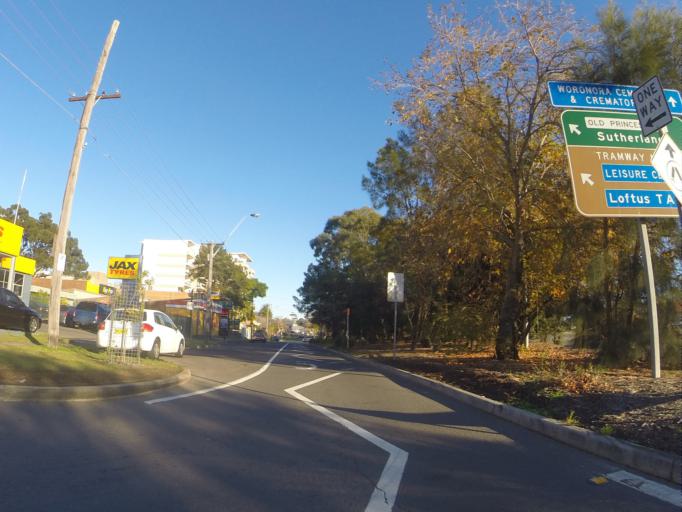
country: AU
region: New South Wales
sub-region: Sutherland Shire
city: Kirrawee
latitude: -34.0298
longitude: 151.0618
